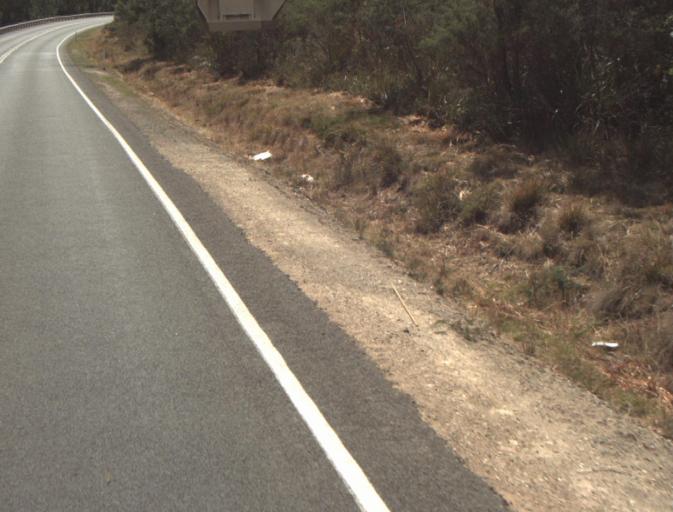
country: AU
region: Tasmania
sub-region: Launceston
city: Mayfield
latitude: -41.3584
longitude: 147.1428
